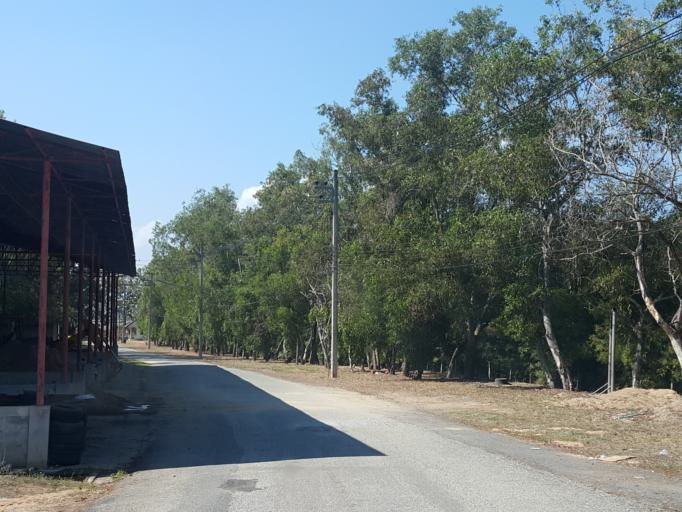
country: TH
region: Chiang Mai
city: Mae Taeng
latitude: 19.0319
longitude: 98.9880
